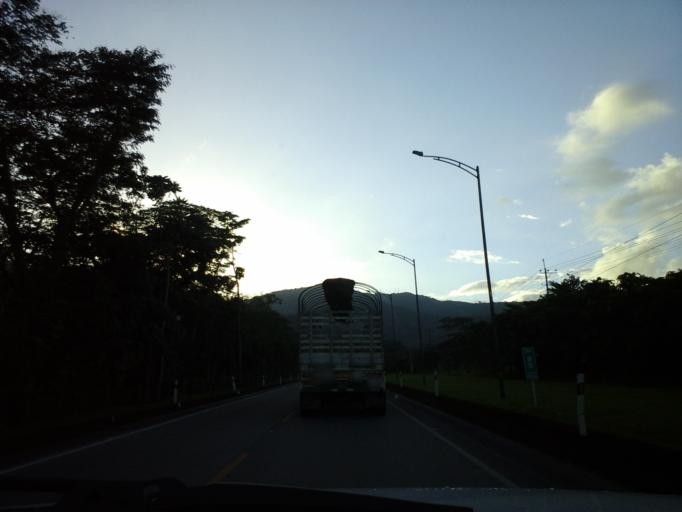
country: CO
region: Meta
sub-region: Villavicencio
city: Villavicencio
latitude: 4.1254
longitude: -73.6500
